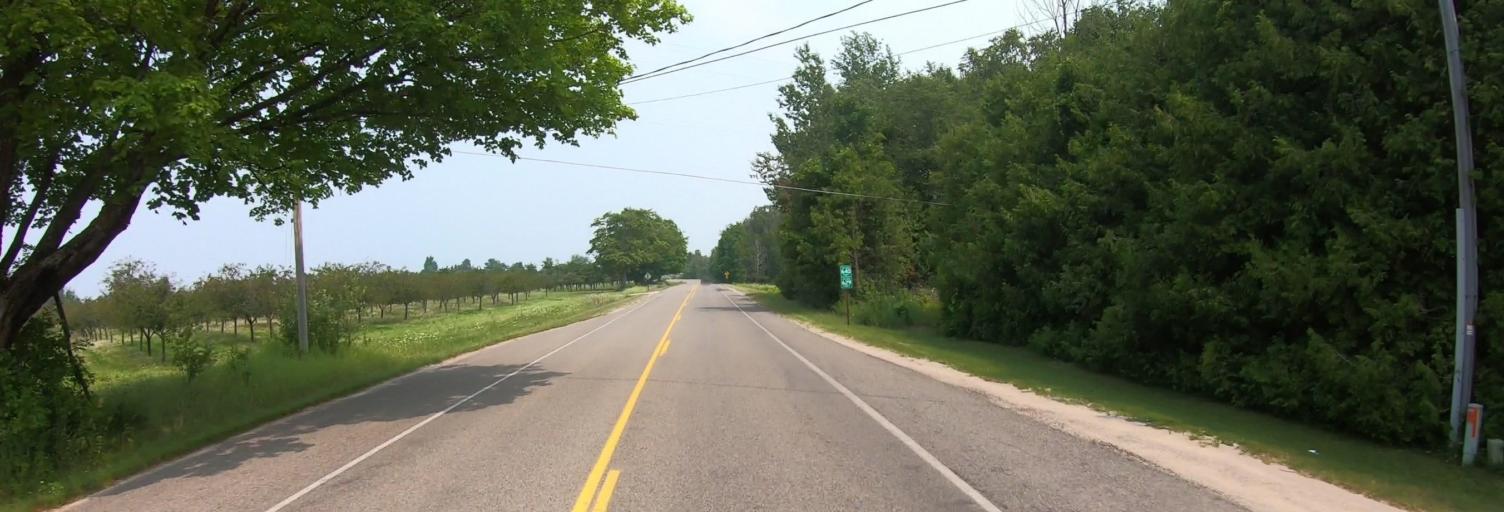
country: US
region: Michigan
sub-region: Leelanau County
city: Leland
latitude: 45.1479
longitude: -85.6139
